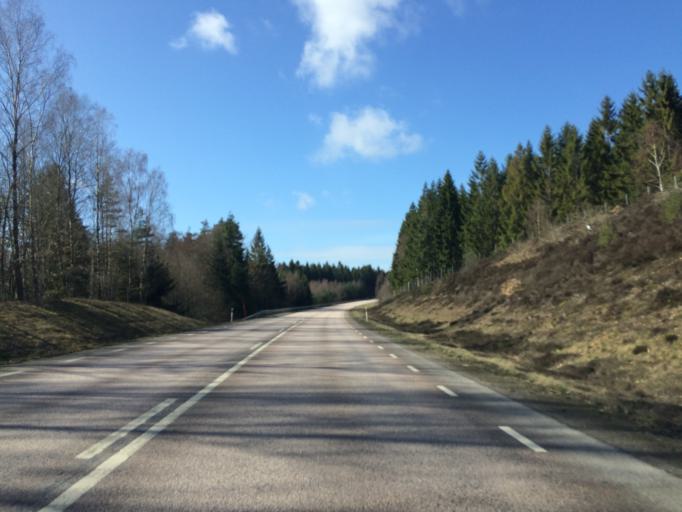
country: SE
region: Halland
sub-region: Laholms Kommun
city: Knared
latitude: 56.5223
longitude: 13.2591
